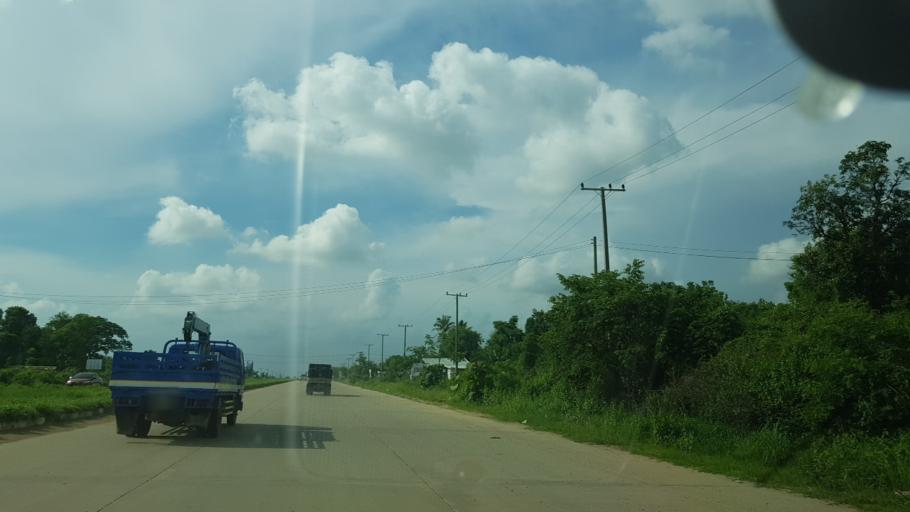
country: TH
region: Nong Khai
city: Nong Khai
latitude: 17.9094
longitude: 102.7201
